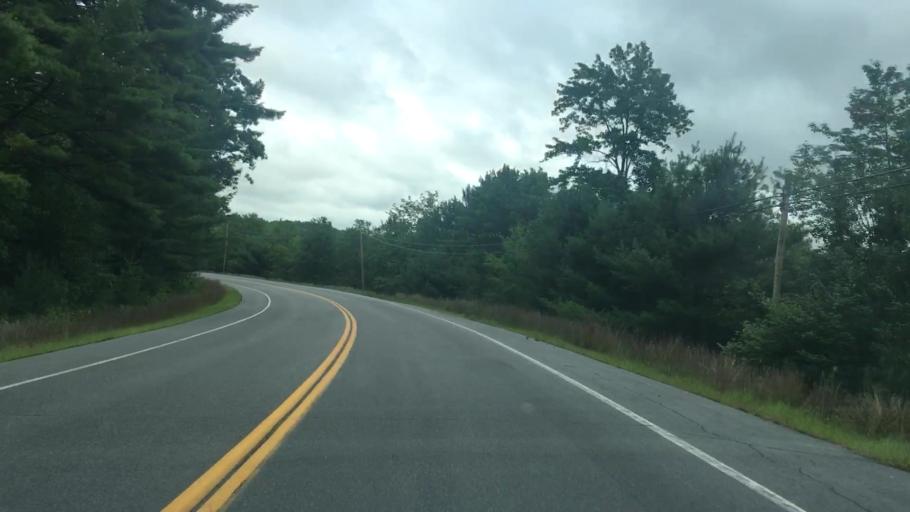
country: US
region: Maine
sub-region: York County
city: Cornish
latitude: 43.7781
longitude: -70.8246
